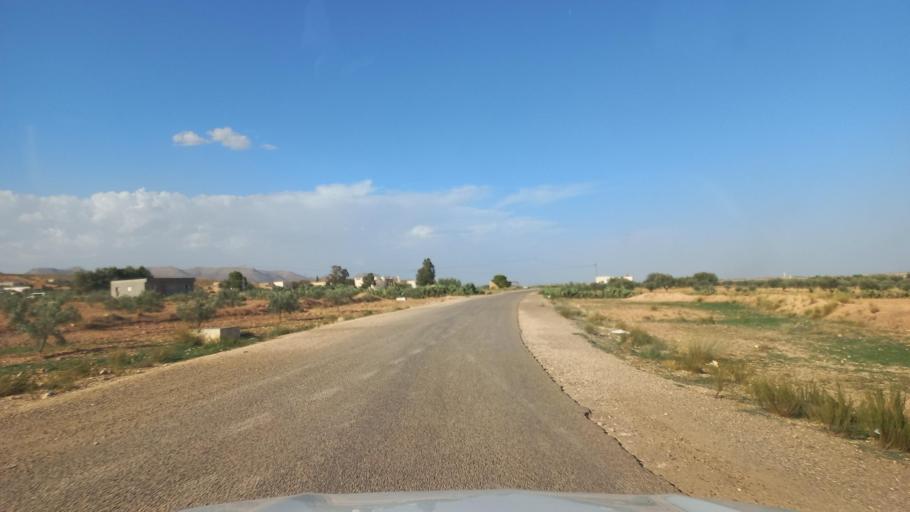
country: TN
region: Al Qasrayn
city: Sbiba
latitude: 35.3728
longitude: 9.0133
